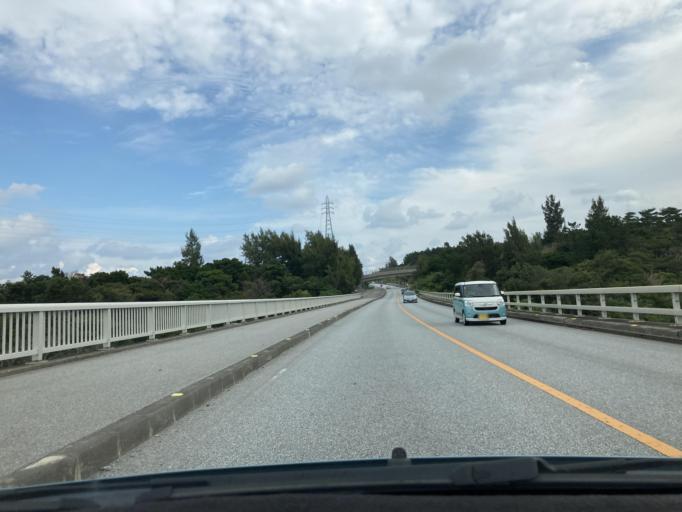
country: JP
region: Okinawa
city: Ishikawa
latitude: 26.4998
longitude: 127.8637
